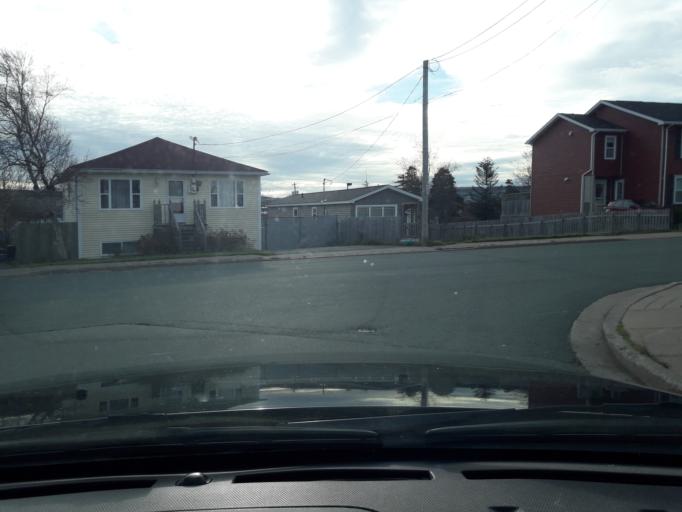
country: CA
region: Newfoundland and Labrador
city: St. John's
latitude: 47.5653
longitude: -52.7615
